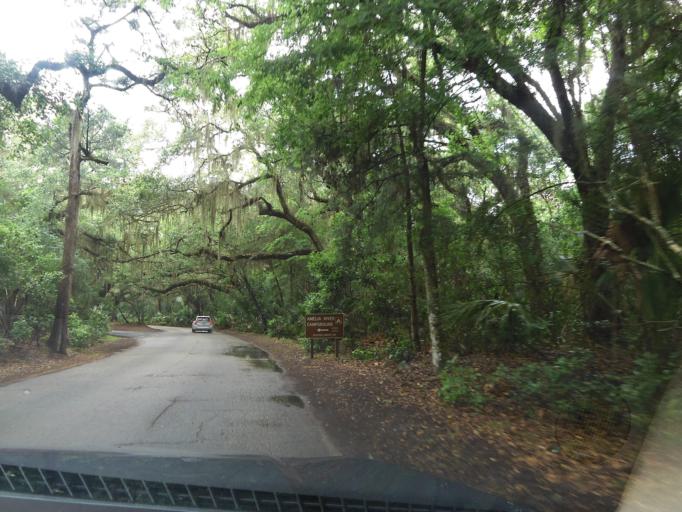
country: US
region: Florida
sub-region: Nassau County
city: Fernandina Beach
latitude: 30.7028
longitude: -81.4490
